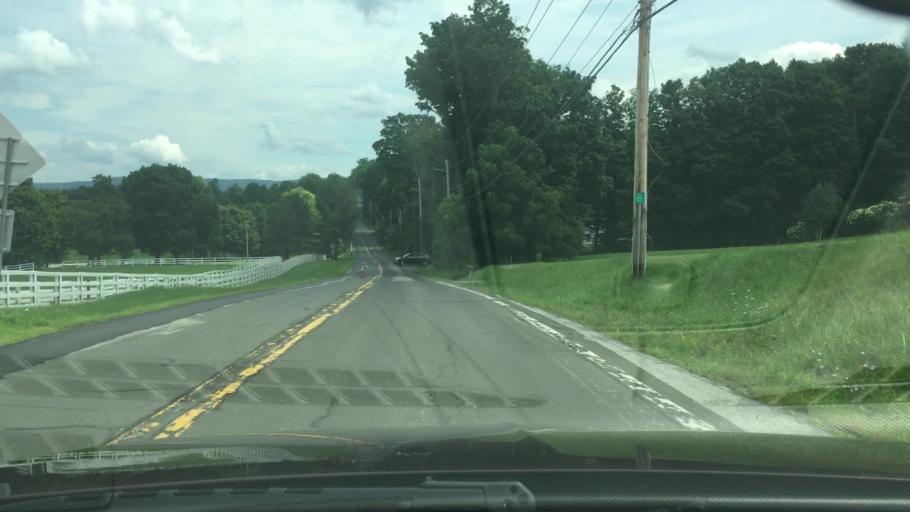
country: US
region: New York
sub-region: Dutchess County
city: Pawling
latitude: 41.5919
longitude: -73.6992
